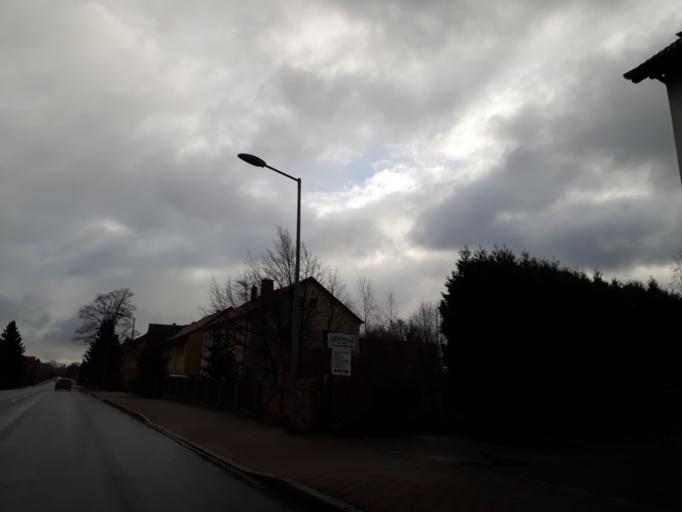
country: DE
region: Saxony
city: Herrnhut
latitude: 51.0236
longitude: 14.7319
